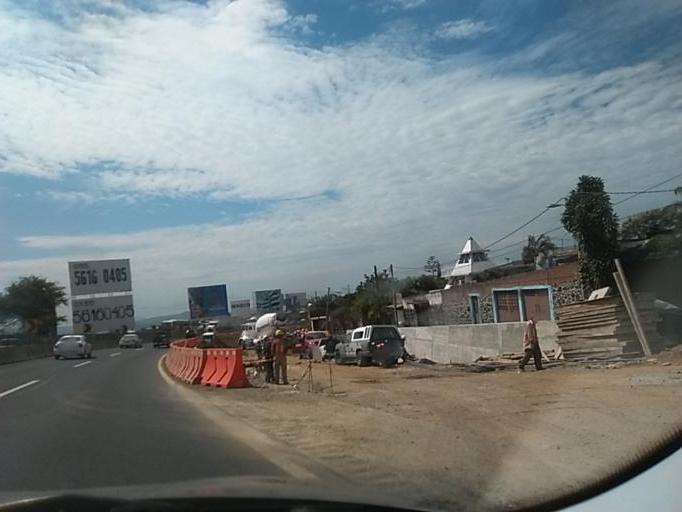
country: MX
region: Morelos
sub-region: Cuernavaca
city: Colonia los Cerritos
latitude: 18.9471
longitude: -99.1875
